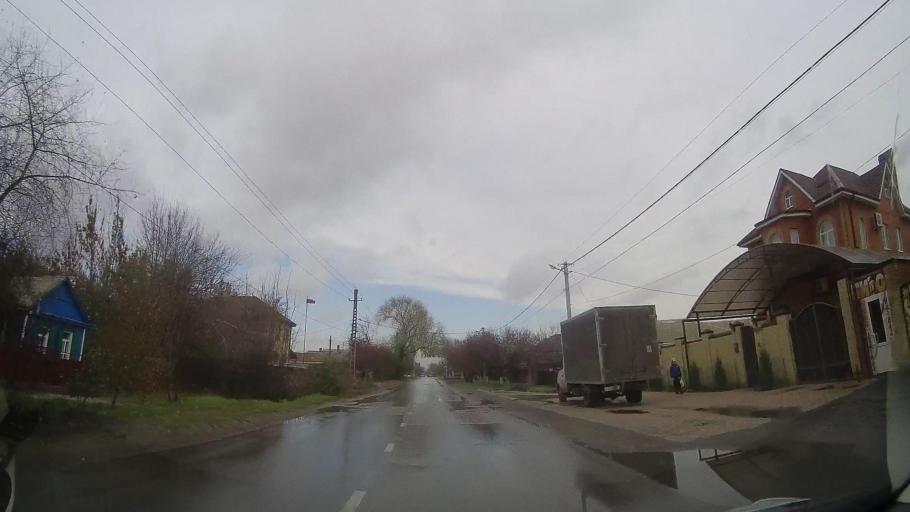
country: RU
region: Rostov
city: Bataysk
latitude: 47.1247
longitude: 39.7682
